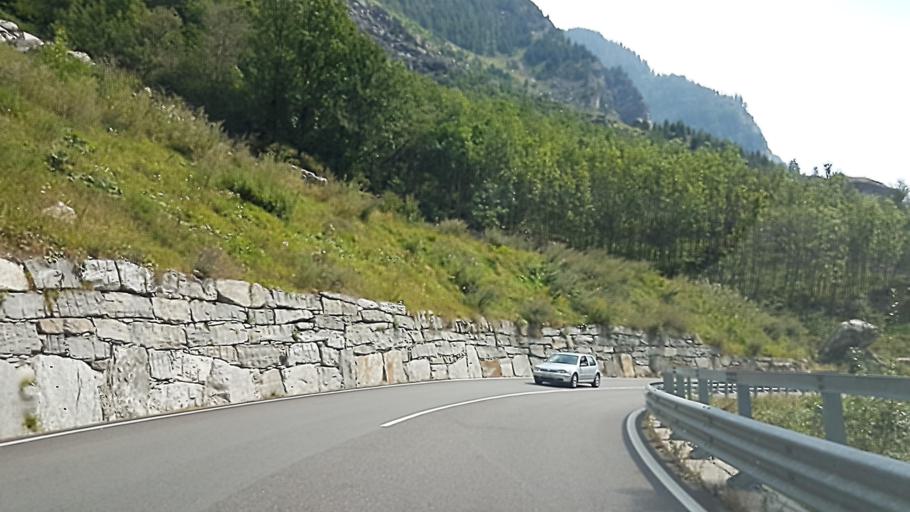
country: IT
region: Lombardy
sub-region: Provincia di Sondrio
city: Campodolcino
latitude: 46.3745
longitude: 9.3605
